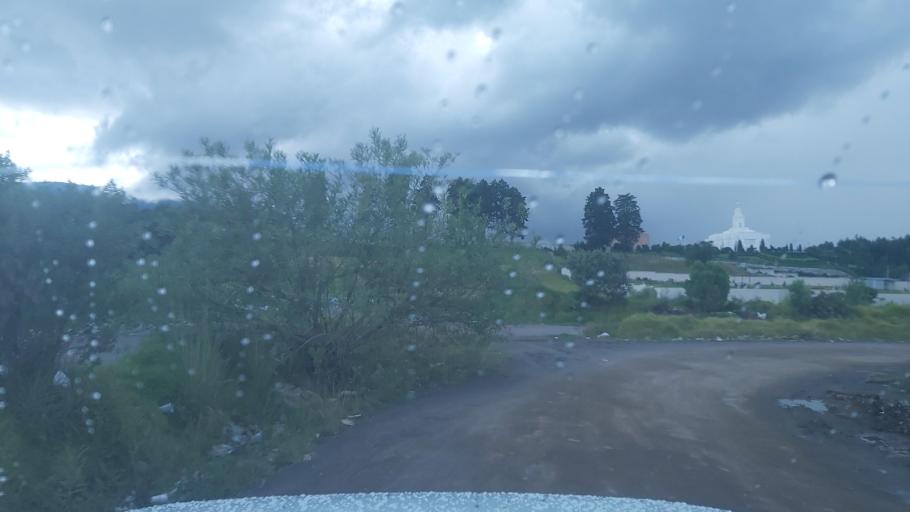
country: GT
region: Quetzaltenango
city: Quetzaltenango
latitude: 14.8452
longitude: -91.5390
